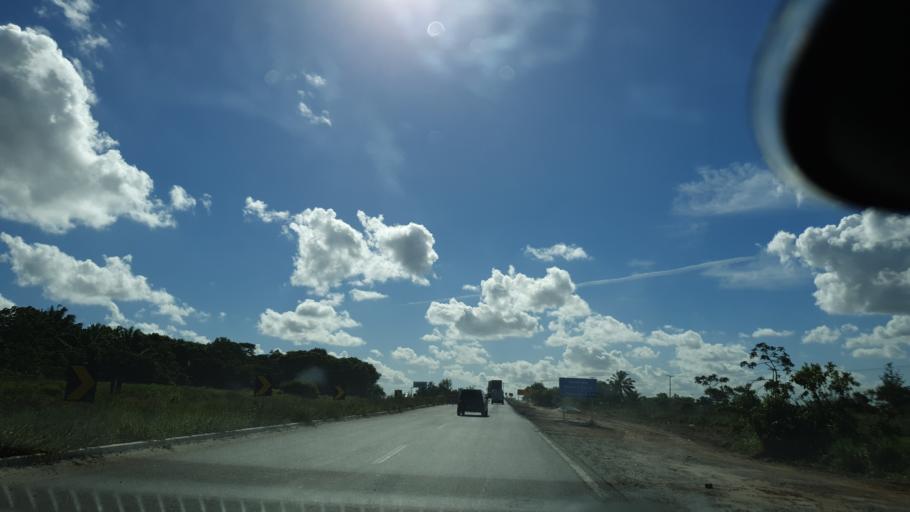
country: BR
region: Bahia
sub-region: Camacari
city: Camacari
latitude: -12.6802
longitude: -38.2837
